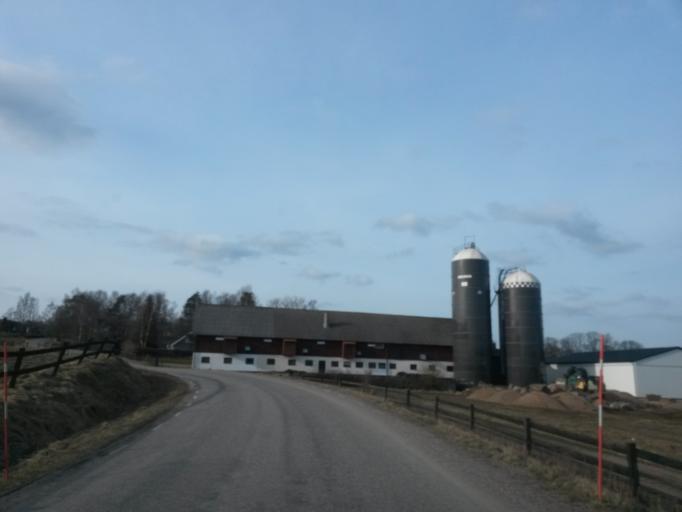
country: SE
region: Vaestra Goetaland
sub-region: Vargarda Kommun
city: Jonstorp
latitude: 57.9942
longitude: 12.7693
